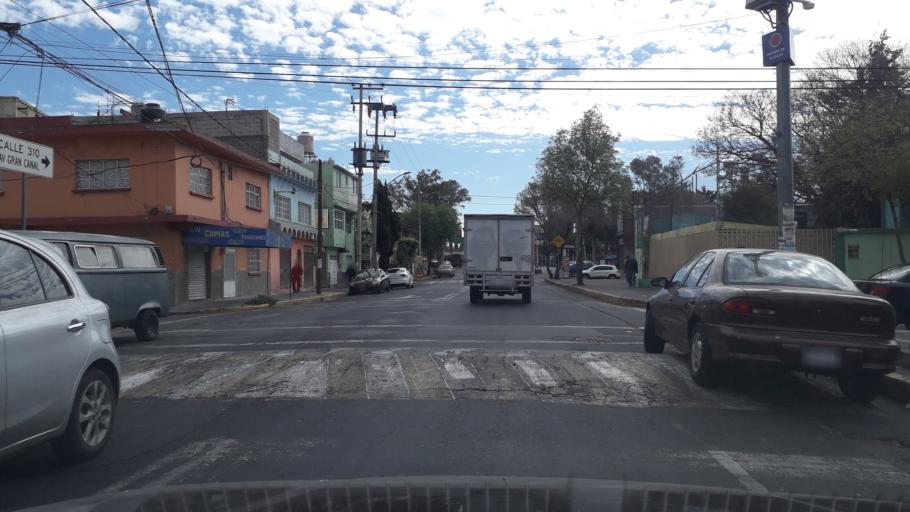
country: MX
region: Mexico City
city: Gustavo A. Madero
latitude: 19.4981
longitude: -99.0913
